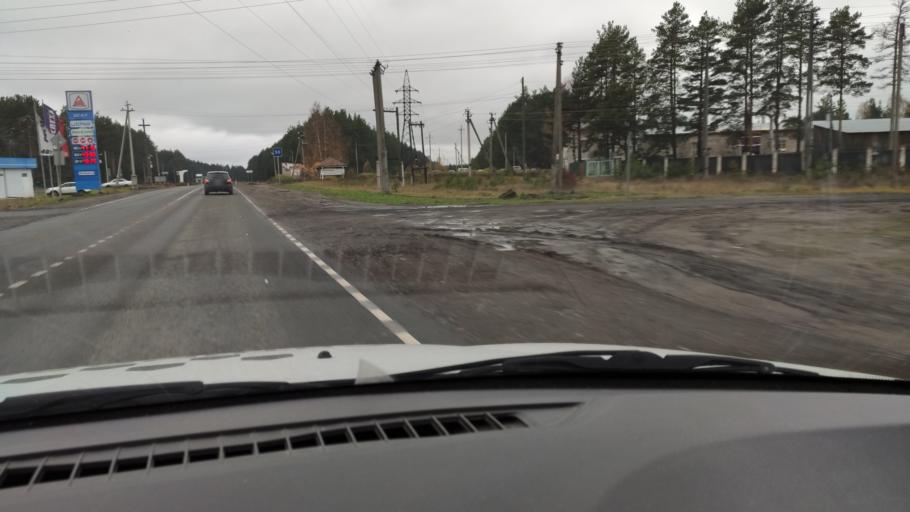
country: RU
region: Kirov
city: Belaya Kholunitsa
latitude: 58.8455
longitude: 50.8149
